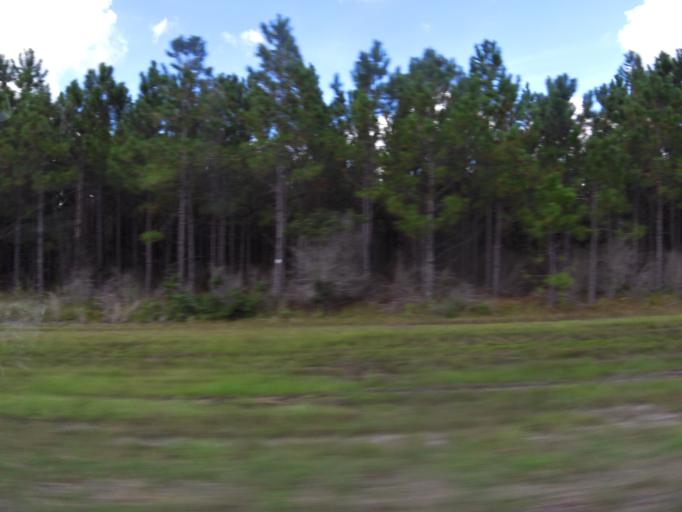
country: US
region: Florida
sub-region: Hamilton County
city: Jasper
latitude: 30.6736
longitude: -82.6659
